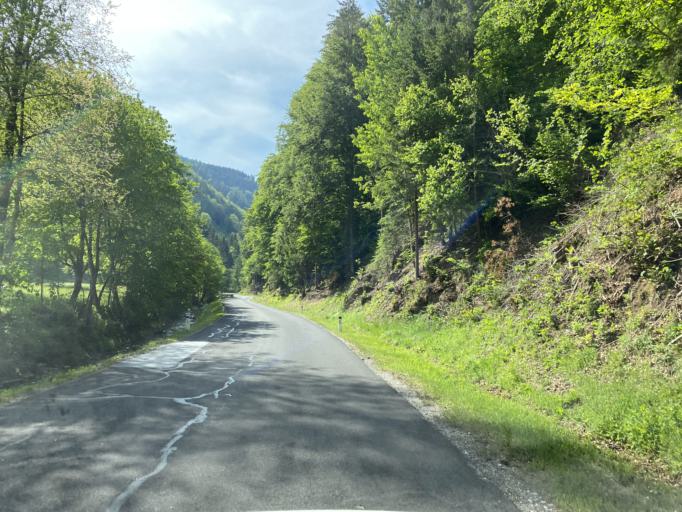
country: AT
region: Styria
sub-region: Politischer Bezirk Weiz
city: Koglhof
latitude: 47.3050
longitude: 15.6679
